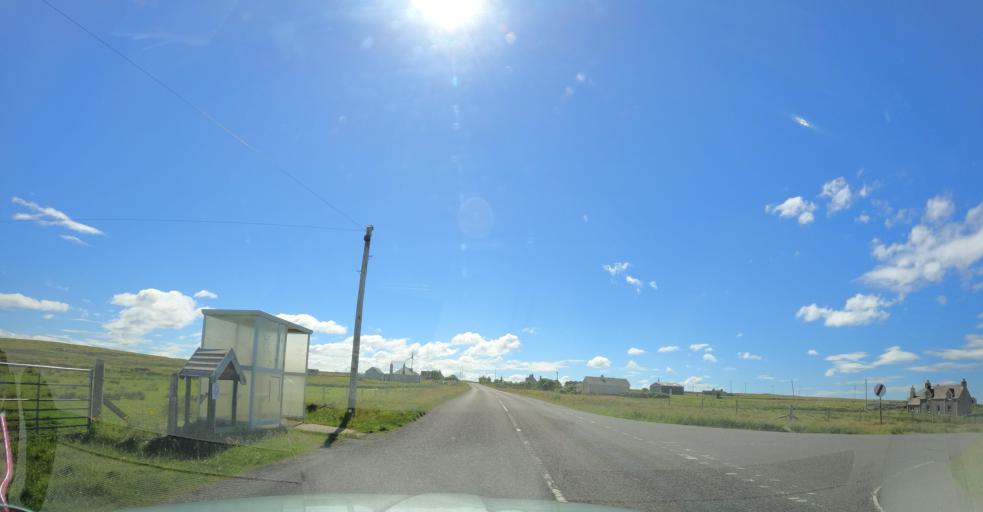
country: GB
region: Scotland
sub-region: Eilean Siar
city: Isle of Lewis
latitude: 58.3915
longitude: -6.4843
